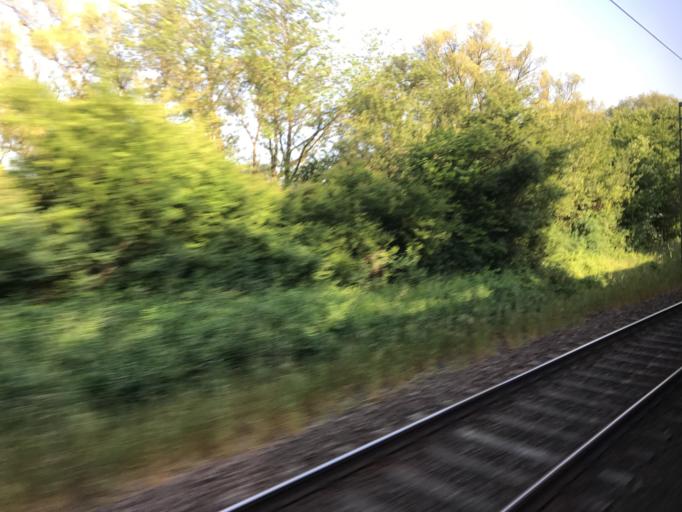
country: DE
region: Saarland
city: Ottweiler
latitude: 49.4204
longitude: 7.1637
